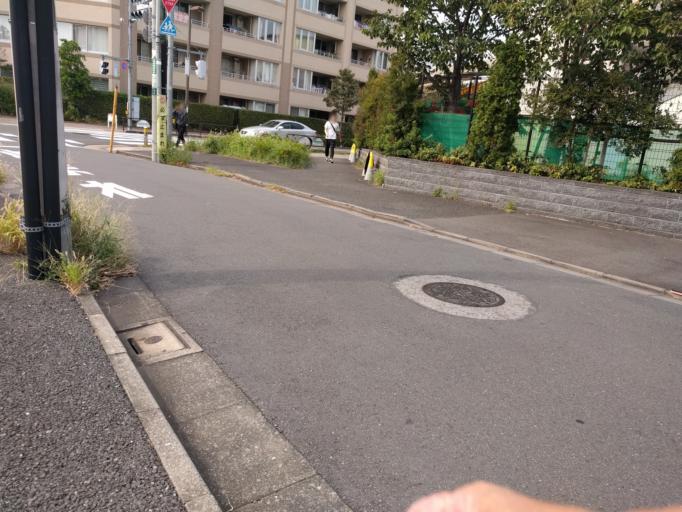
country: JP
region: Tokyo
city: Tokyo
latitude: 35.6500
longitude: 139.6522
